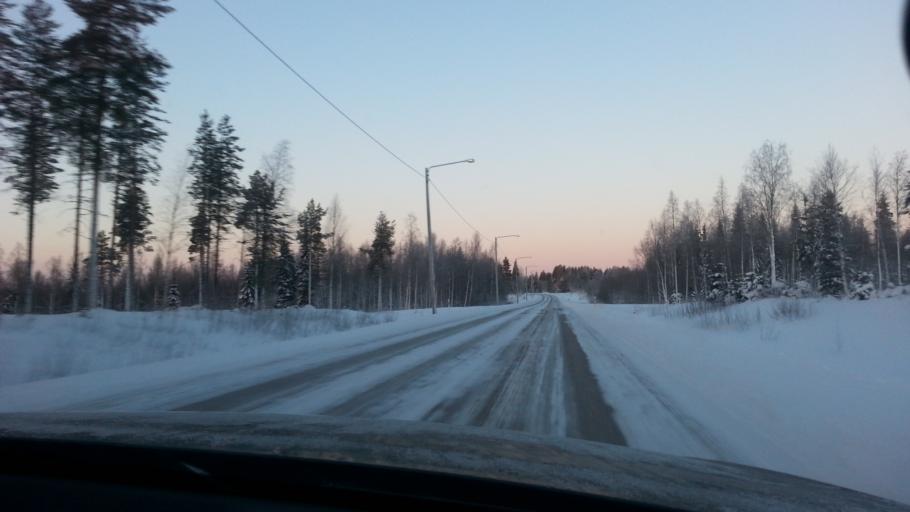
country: FI
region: Lapland
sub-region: Tunturi-Lappi
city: Kittilae
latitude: 67.0363
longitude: 25.1038
